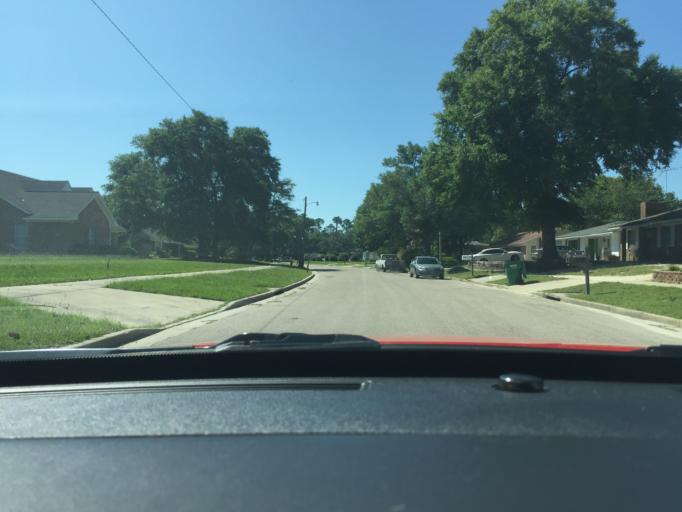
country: US
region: Mississippi
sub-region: Harrison County
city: D'Iberville
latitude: 30.3937
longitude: -88.9882
